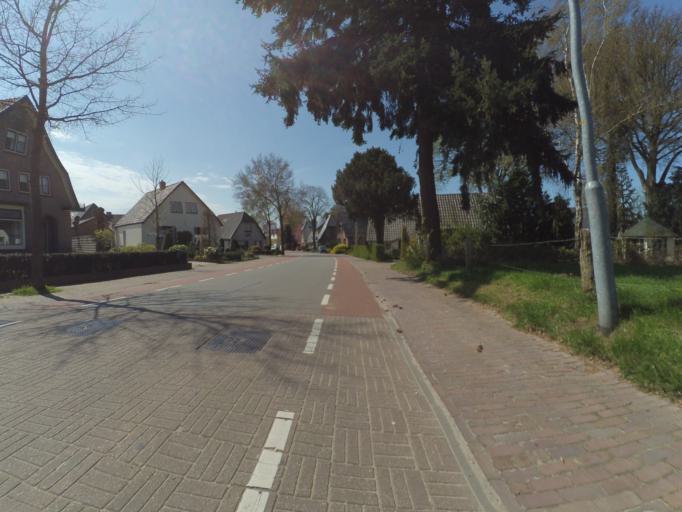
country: NL
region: Gelderland
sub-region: Gemeente Apeldoorn
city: Uddel
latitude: 52.2942
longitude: 5.7915
